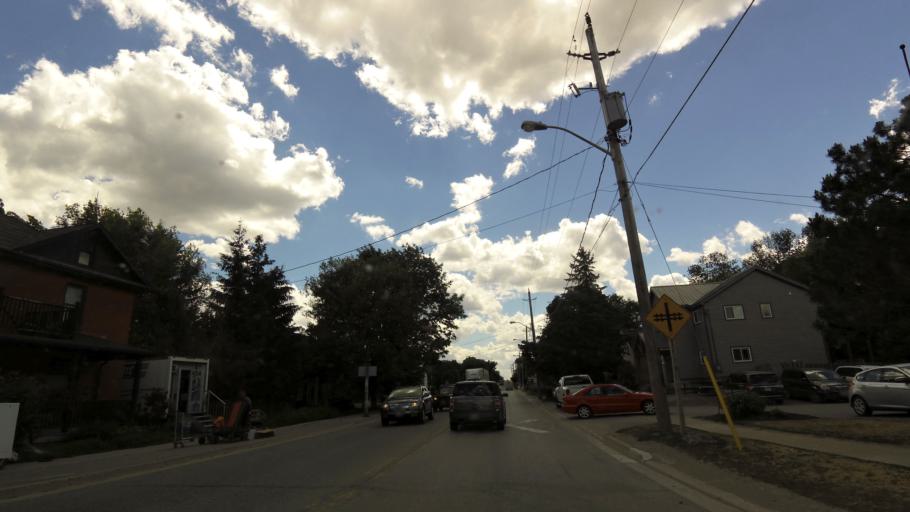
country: CA
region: Ontario
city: Uxbridge
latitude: 44.0371
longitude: -79.1963
